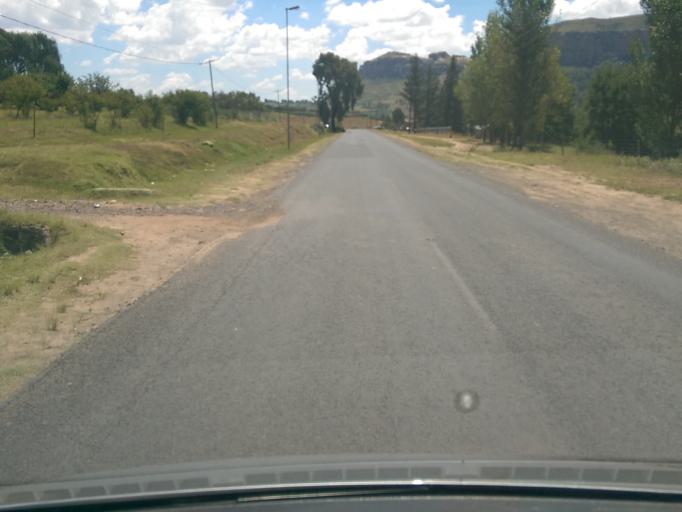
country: LS
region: Maseru
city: Nako
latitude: -29.4416
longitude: 27.7066
